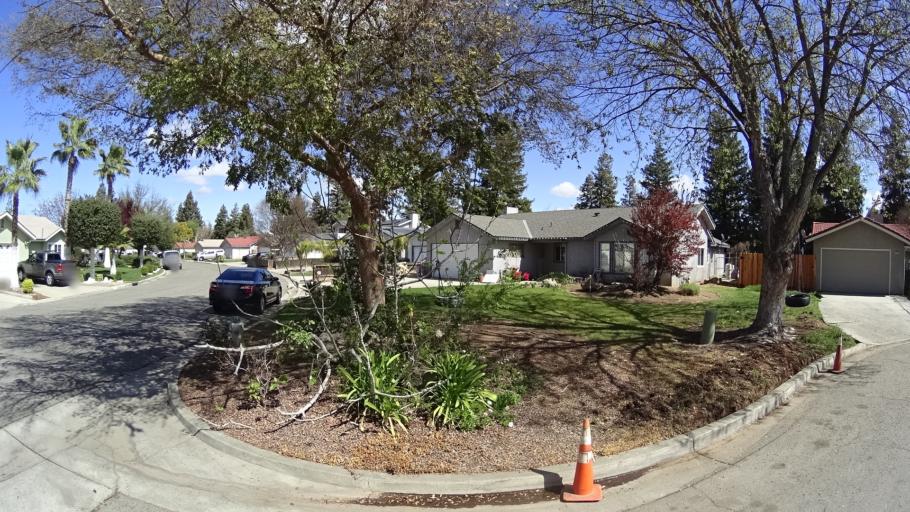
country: US
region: California
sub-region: Fresno County
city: West Park
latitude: 36.8261
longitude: -119.8847
